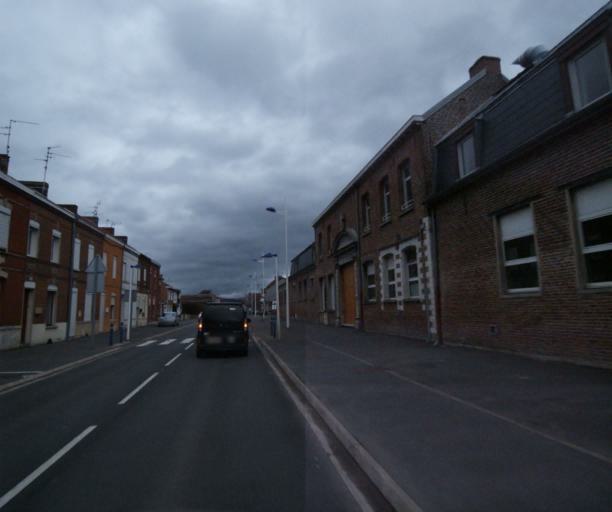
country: FR
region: Nord-Pas-de-Calais
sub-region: Departement du Nord
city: Raismes
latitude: 50.3940
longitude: 3.4857
